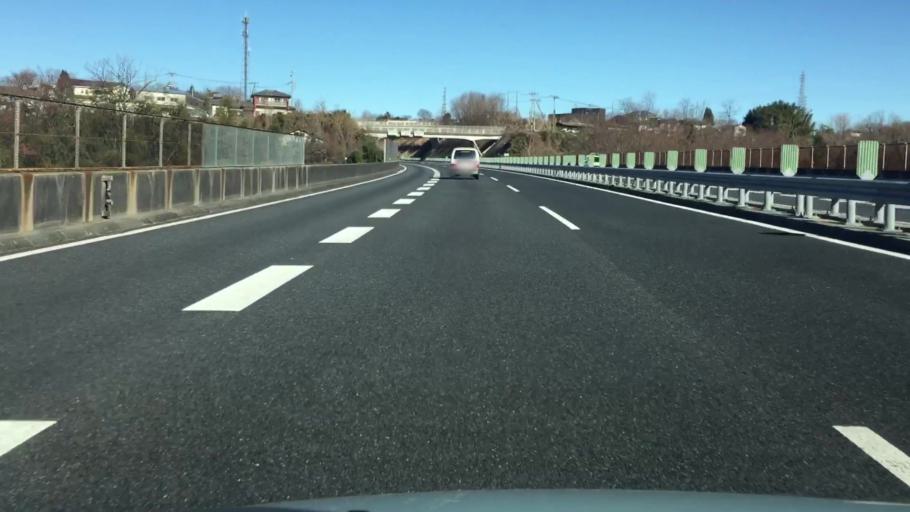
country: JP
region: Gunma
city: Shibukawa
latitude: 36.4905
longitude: 139.0308
